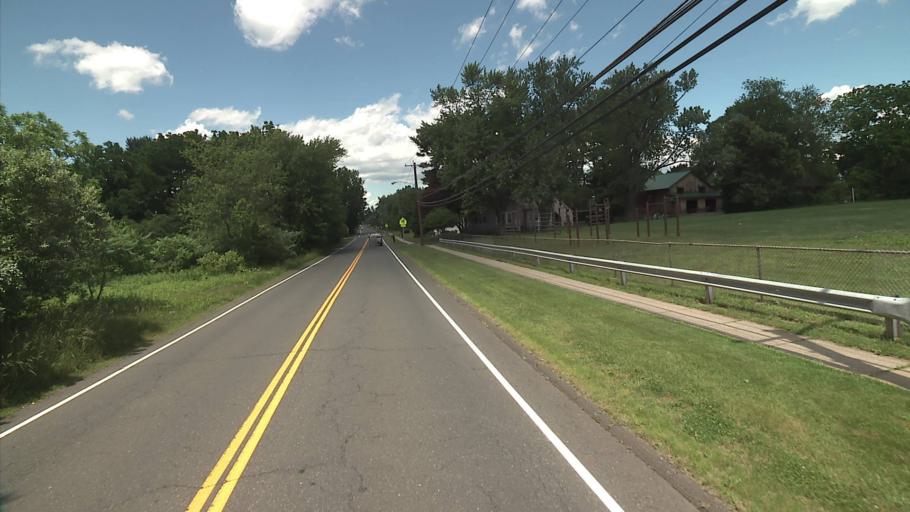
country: US
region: Connecticut
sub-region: Hartford County
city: Hazardville
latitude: 41.9939
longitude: -72.5399
